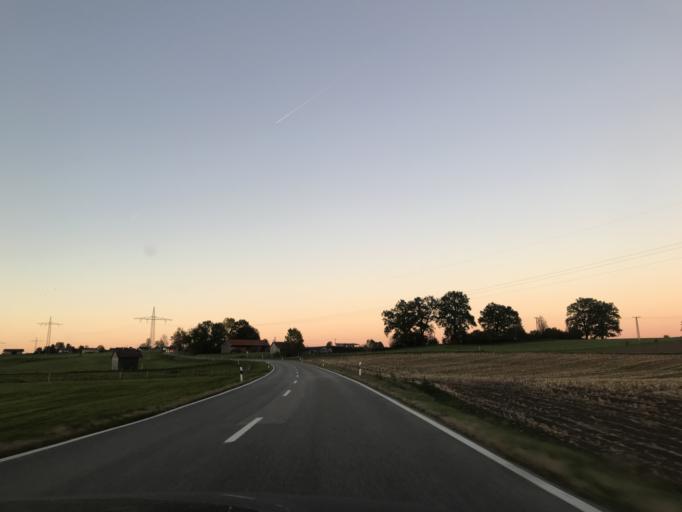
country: DE
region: Bavaria
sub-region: Upper Bavaria
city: Spatzenhausen
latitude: 47.7064
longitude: 11.2104
